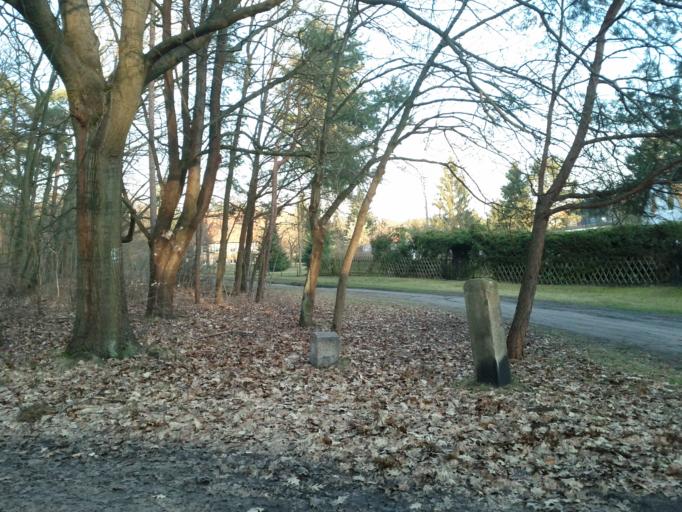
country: DE
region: Brandenburg
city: Grunheide
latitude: 52.4245
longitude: 13.8007
